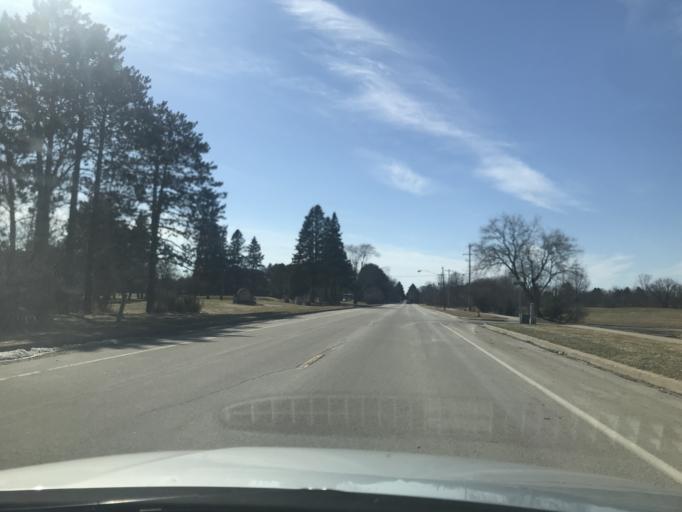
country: US
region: Wisconsin
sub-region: Marinette County
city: Marinette
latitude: 45.1118
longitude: -87.6445
